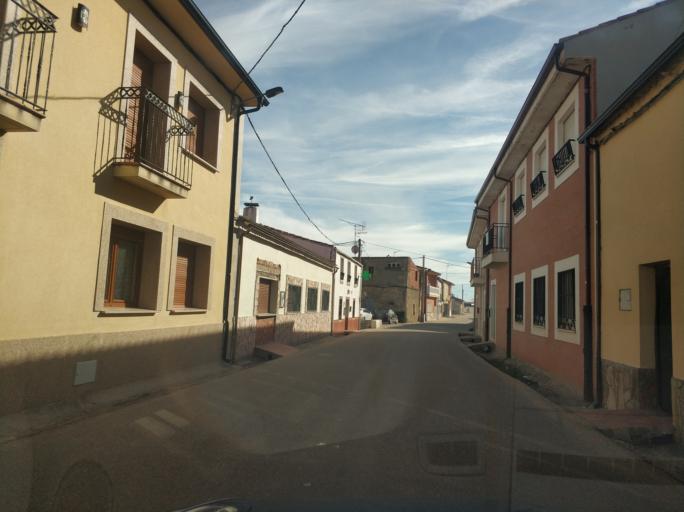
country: ES
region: Castille and Leon
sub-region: Provincia de Zamora
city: Cuelgamures
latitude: 41.2552
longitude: -5.7105
